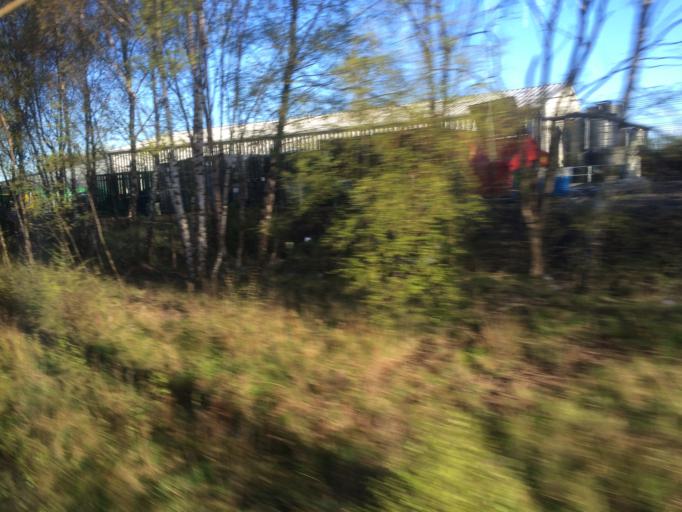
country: GB
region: Scotland
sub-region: South Lanarkshire
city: Rutherglen
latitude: 55.8312
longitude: -4.1716
